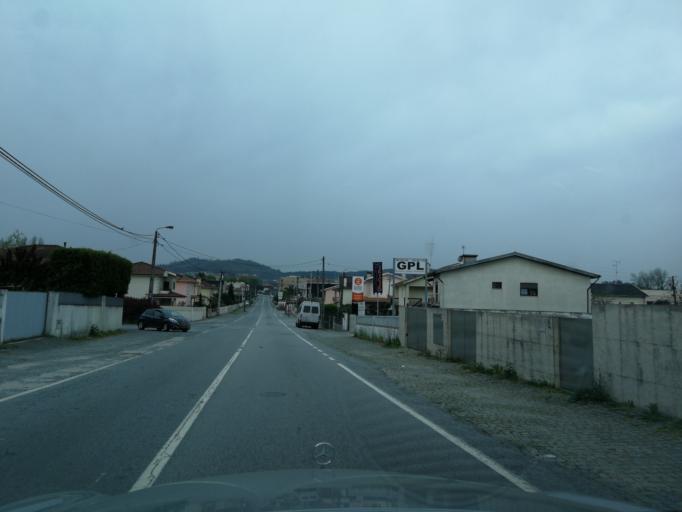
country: PT
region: Braga
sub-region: Braga
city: Braga
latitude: 41.5630
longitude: -8.4427
